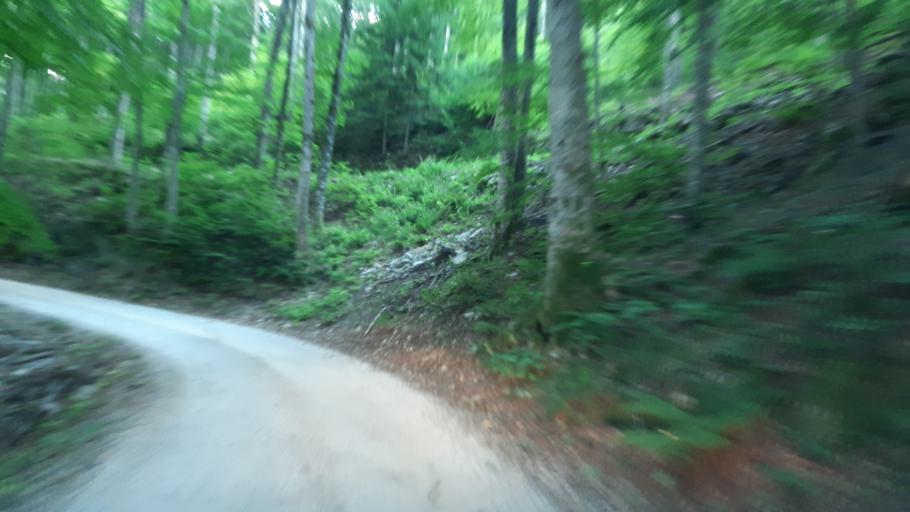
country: SI
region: Dolenjske Toplice
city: Dolenjske Toplice
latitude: 45.6822
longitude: 15.0076
